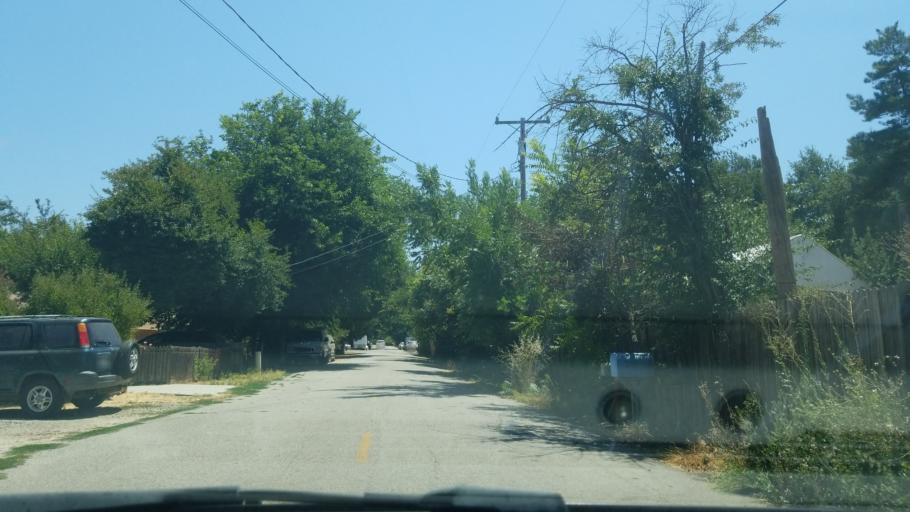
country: US
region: California
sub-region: San Luis Obispo County
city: Atascadero
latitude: 35.5057
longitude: -120.6659
